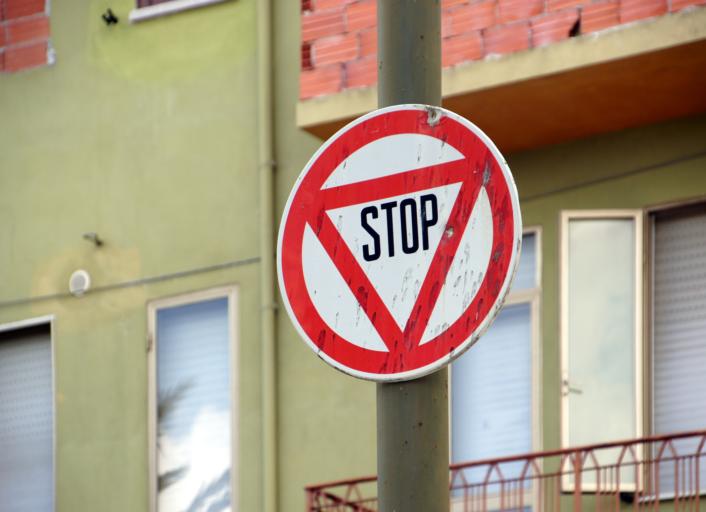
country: IT
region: Sardinia
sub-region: Provincia di Nuoro
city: Orgosolo
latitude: 40.2048
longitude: 9.3504
